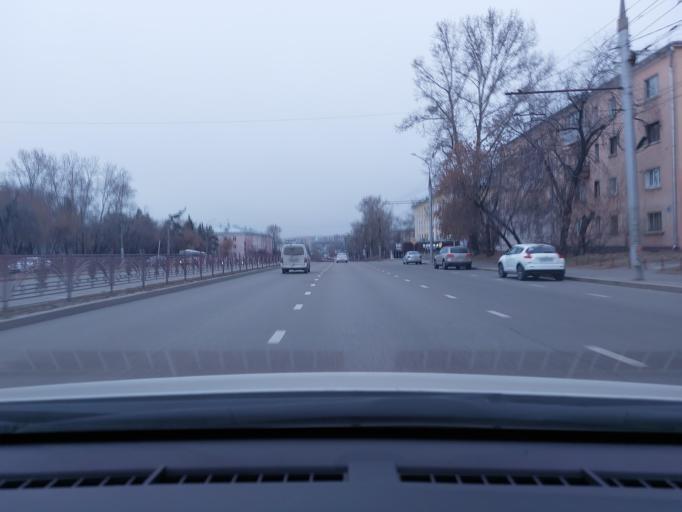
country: RU
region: Irkutsk
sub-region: Irkutskiy Rayon
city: Irkutsk
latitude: 52.2615
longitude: 104.2604
